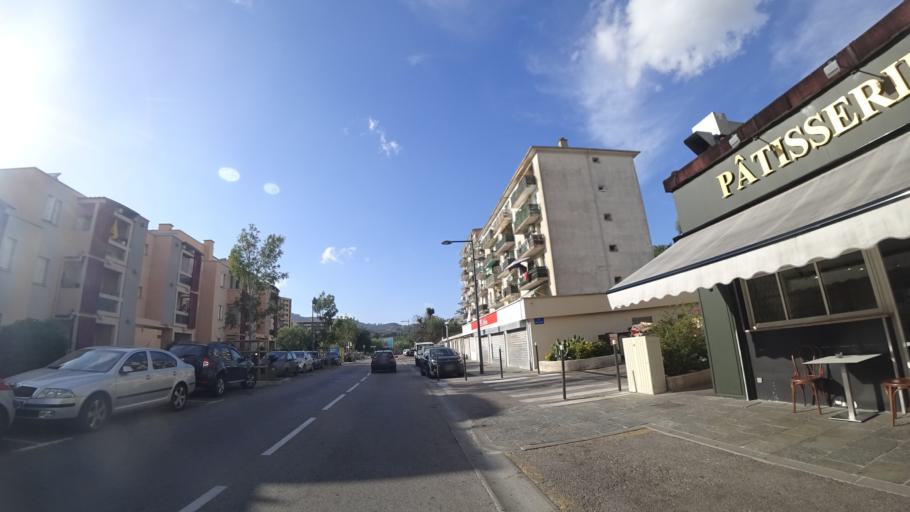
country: FR
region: Corsica
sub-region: Departement de la Corse-du-Sud
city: Ajaccio
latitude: 41.9356
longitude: 8.7432
